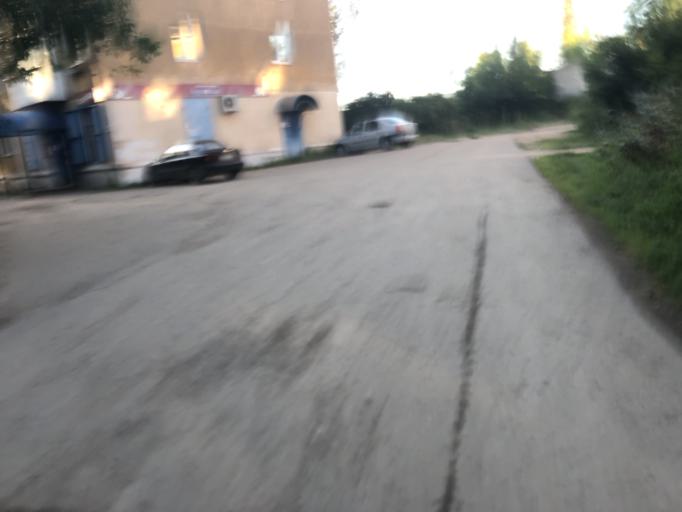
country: RU
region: Tverskaya
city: Rzhev
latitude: 56.2410
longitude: 34.3199
